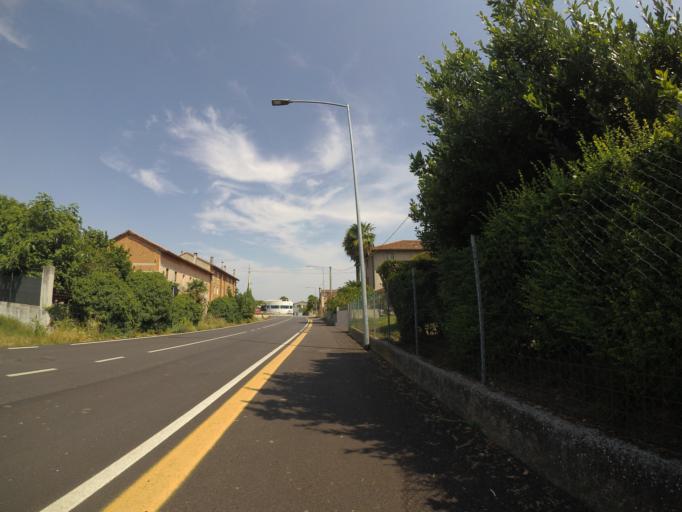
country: IT
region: Friuli Venezia Giulia
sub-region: Provincia di Pordenone
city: Rosa
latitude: 45.9227
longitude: 12.8744
